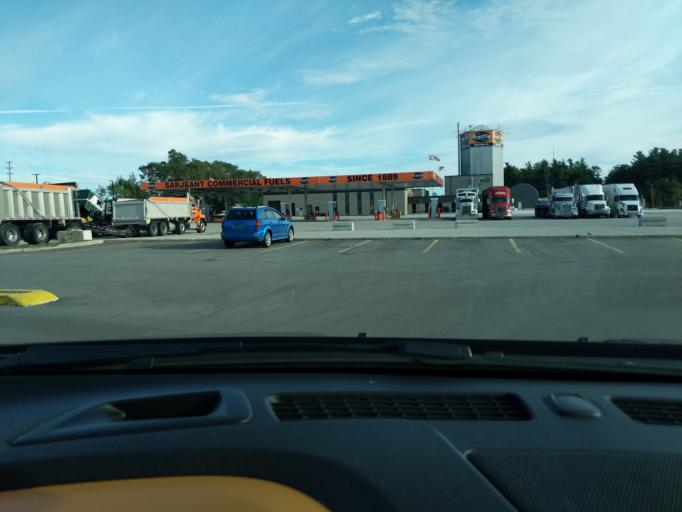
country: CA
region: Ontario
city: Barrie
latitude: 44.3770
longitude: -79.7155
